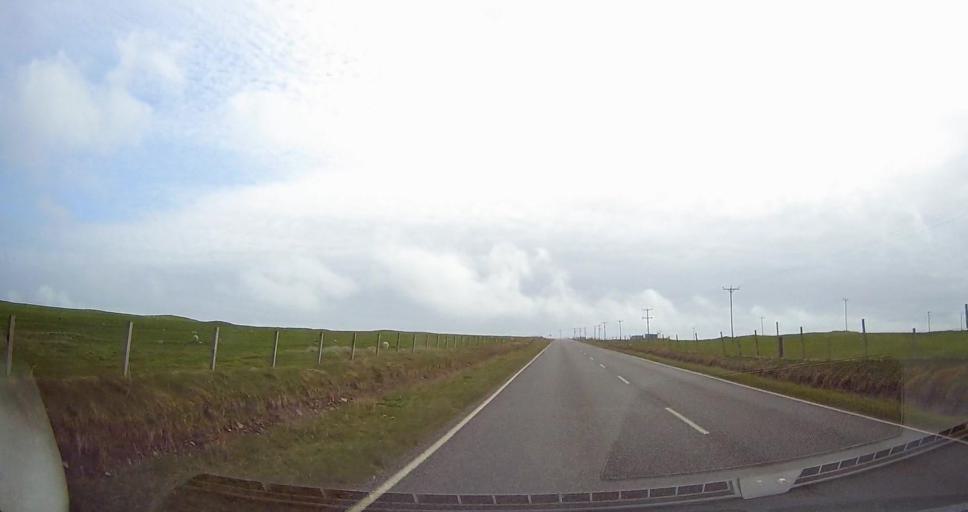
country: GB
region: Scotland
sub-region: Shetland Islands
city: Sandwick
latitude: 59.9016
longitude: -1.3031
